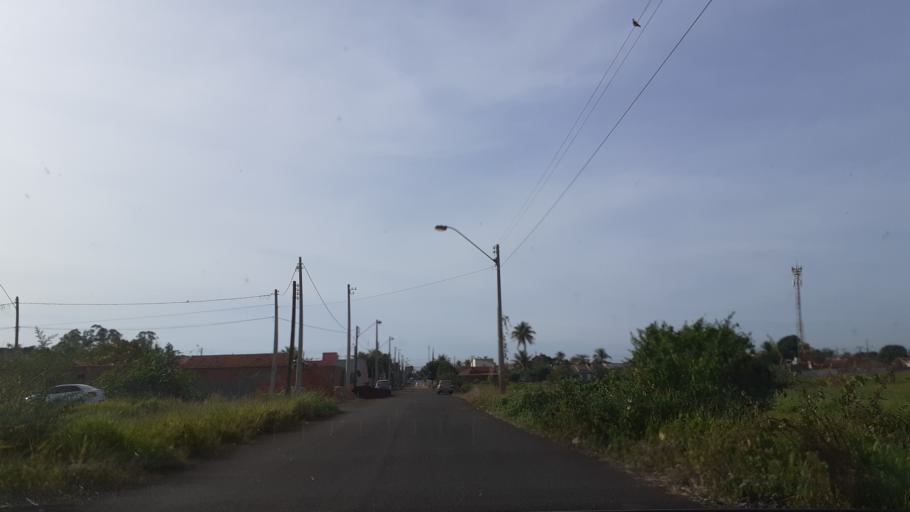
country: BR
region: Goias
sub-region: Itumbiara
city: Itumbiara
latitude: -18.4147
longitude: -49.2480
